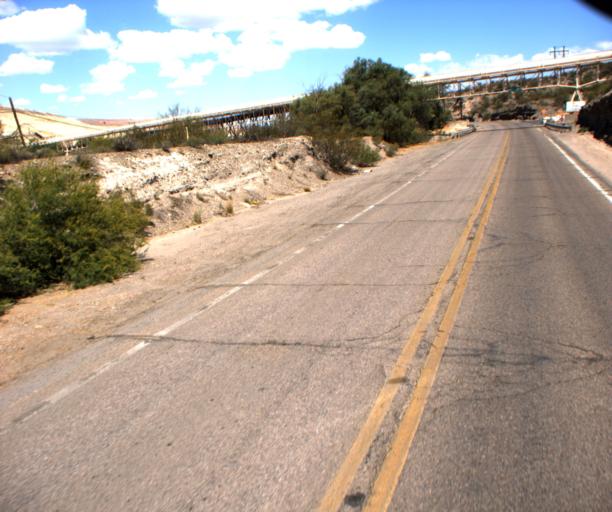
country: US
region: Arizona
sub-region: Pinal County
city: Kearny
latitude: 33.0013
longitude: -110.7893
